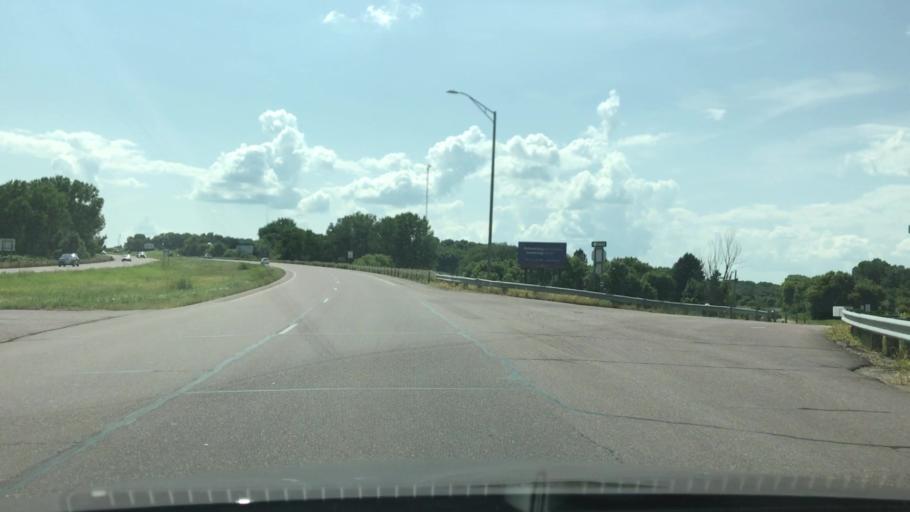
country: US
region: Minnesota
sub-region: Nicollet County
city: North Mankato
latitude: 44.1521
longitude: -94.0720
